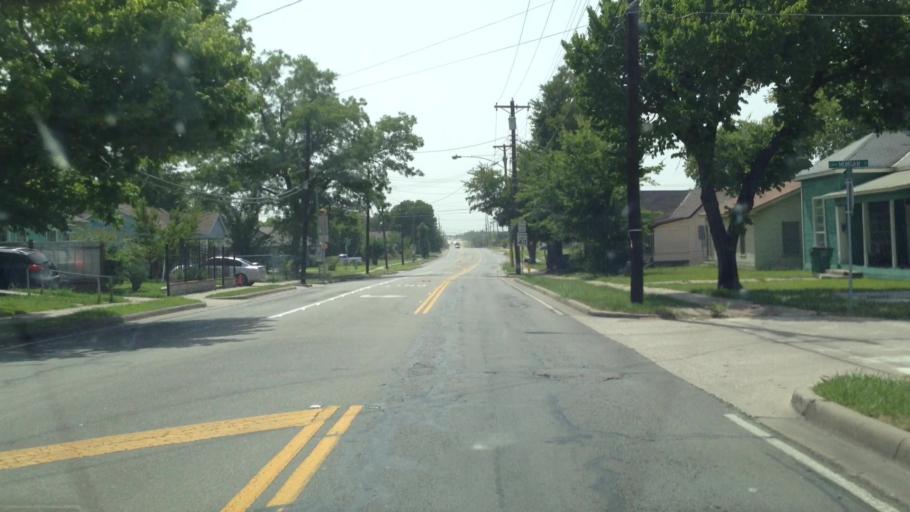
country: US
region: Texas
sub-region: Hunt County
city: Greenville
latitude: 33.1402
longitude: -96.1269
